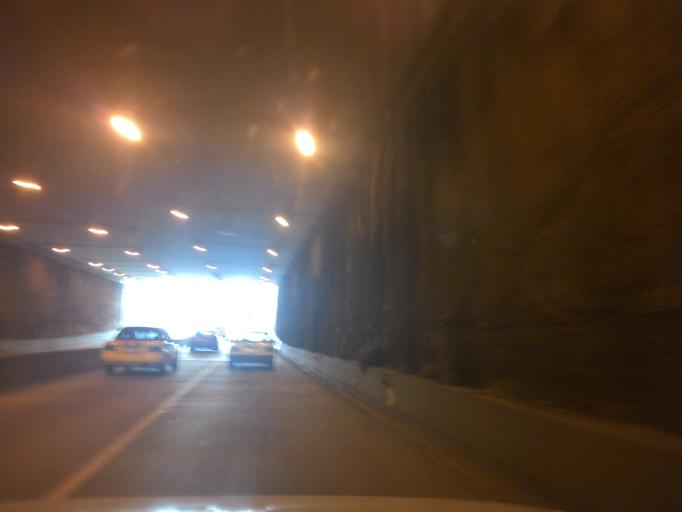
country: MX
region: Jalisco
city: Zapopan2
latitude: 20.6856
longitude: -103.4428
